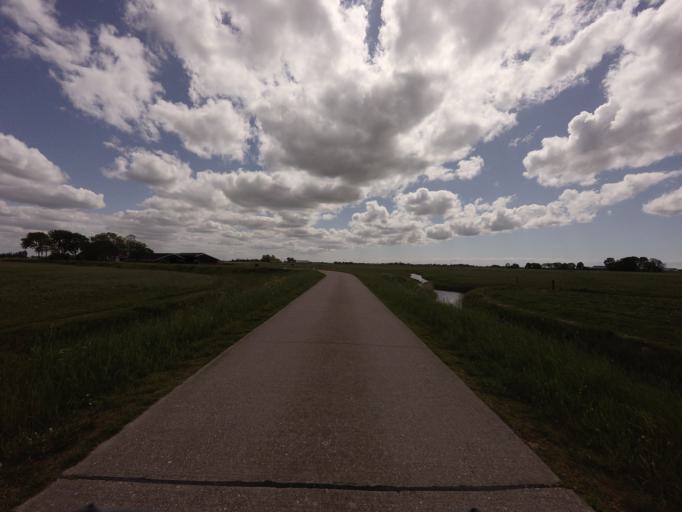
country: NL
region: Friesland
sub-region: Gemeente Franekeradeel
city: Tzum
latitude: 53.1273
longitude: 5.5517
